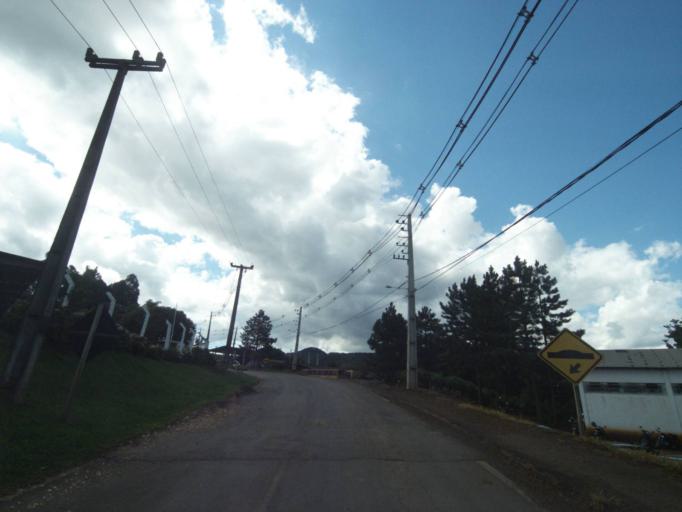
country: BR
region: Parana
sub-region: Uniao Da Vitoria
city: Uniao da Vitoria
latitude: -26.1531
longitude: -51.5389
